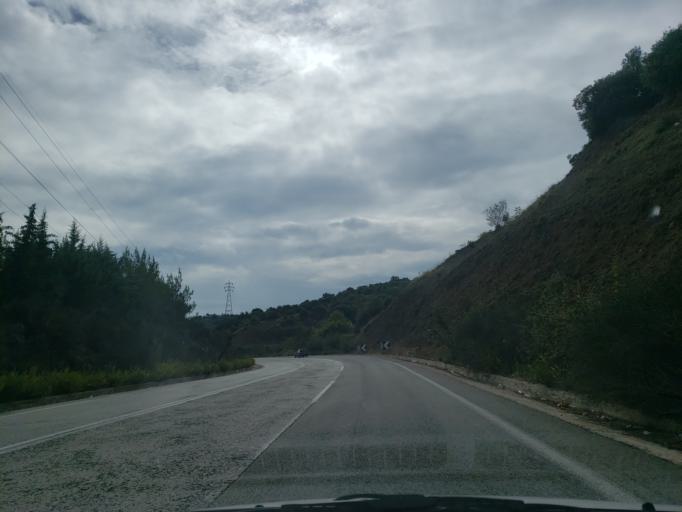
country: GR
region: Central Greece
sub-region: Nomos Fthiotidos
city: Stavros
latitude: 38.9945
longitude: 22.3717
